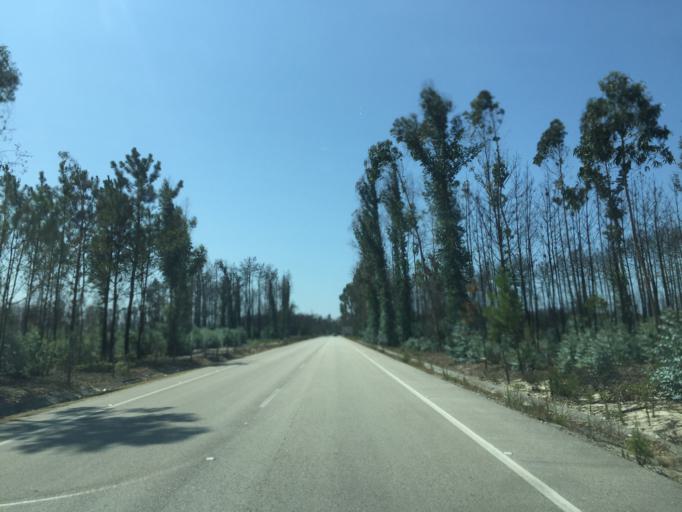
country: PT
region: Coimbra
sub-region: Mira
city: Mira
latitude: 40.3364
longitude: -8.7447
